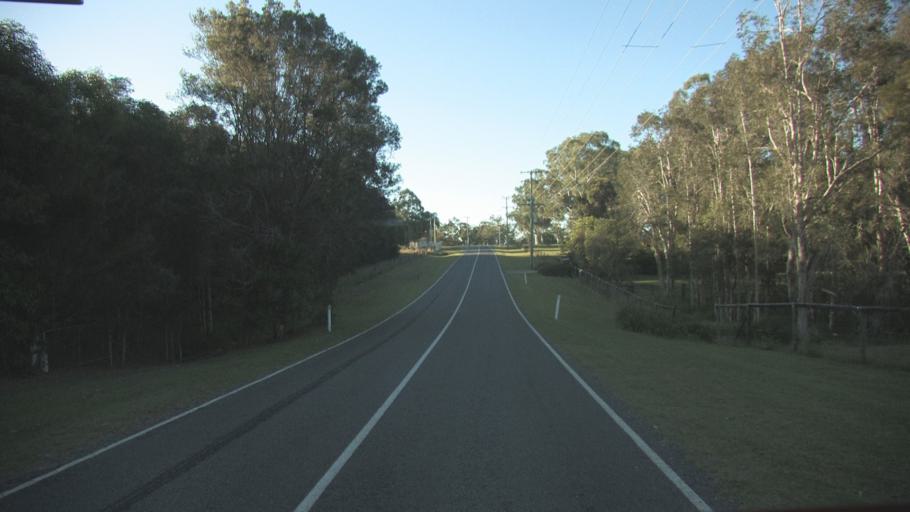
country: AU
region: Queensland
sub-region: Redland
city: Redland Bay
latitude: -27.6628
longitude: 153.2769
